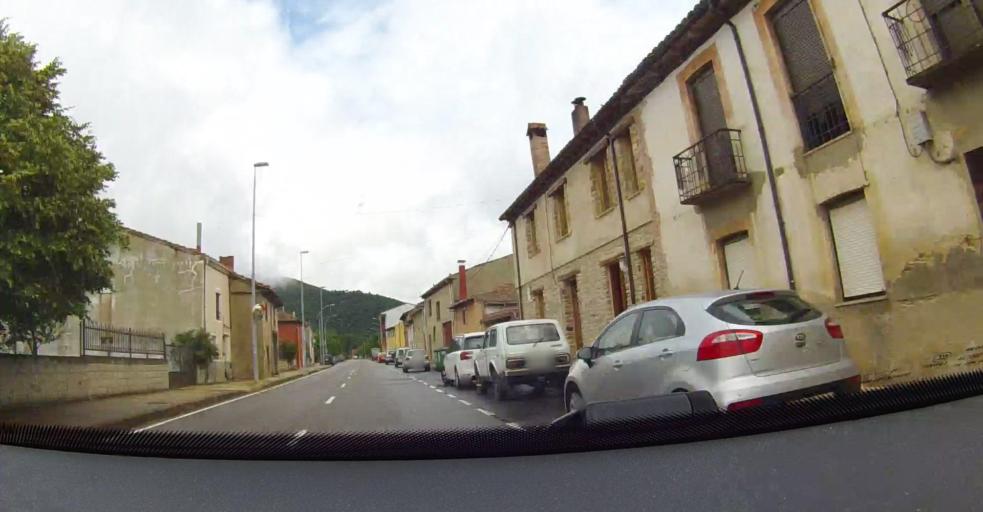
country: ES
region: Castille and Leon
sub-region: Provincia de Leon
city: Bonar
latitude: 42.8723
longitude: -5.3213
